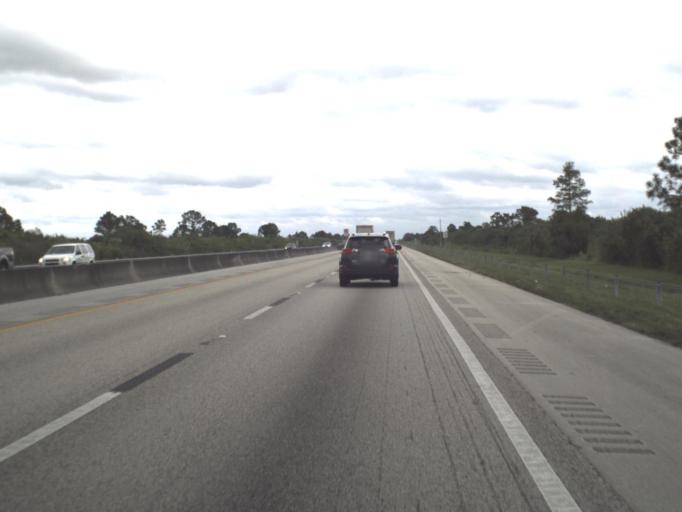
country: US
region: Florida
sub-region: Martin County
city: Hobe Sound
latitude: 27.0167
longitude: -80.2216
